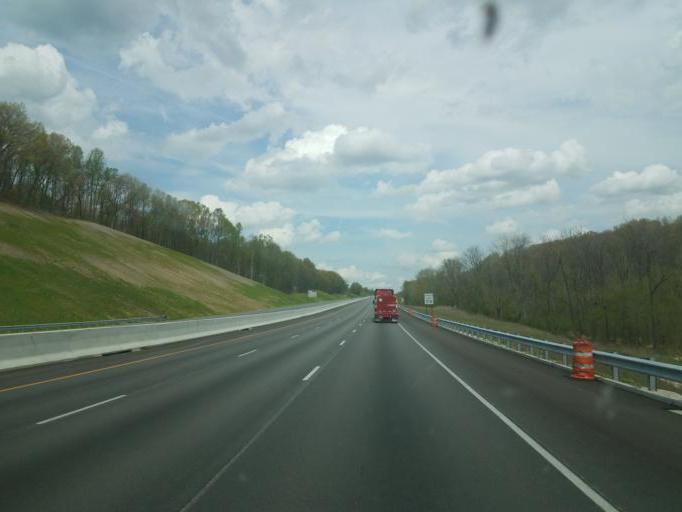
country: US
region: Kentucky
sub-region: Hart County
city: Munfordville
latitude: 37.3107
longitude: -85.9038
